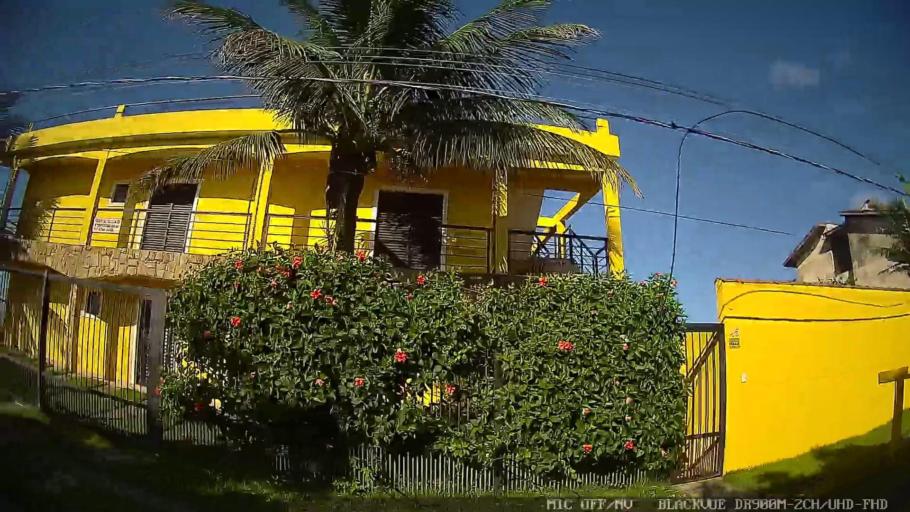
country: BR
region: Sao Paulo
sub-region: Peruibe
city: Peruibe
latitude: -24.2731
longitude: -46.9325
